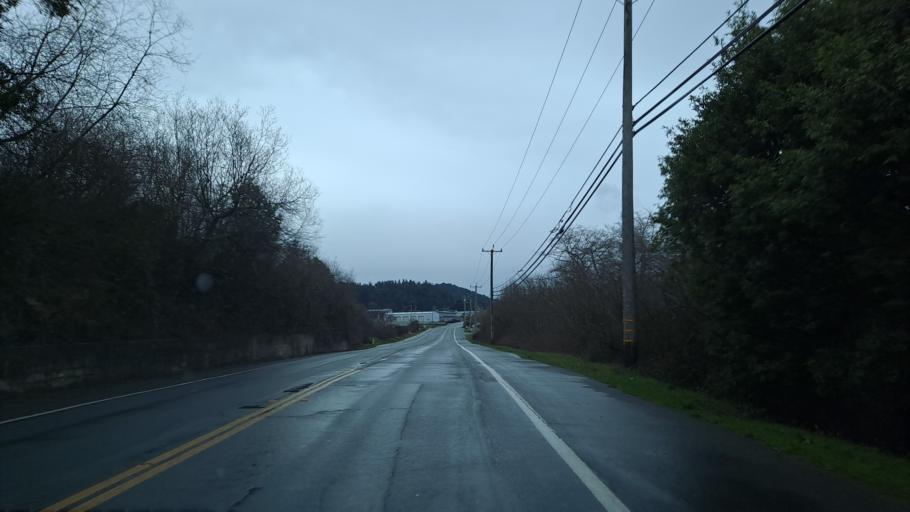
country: US
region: California
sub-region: Humboldt County
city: Fortuna
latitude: 40.5880
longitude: -124.1329
